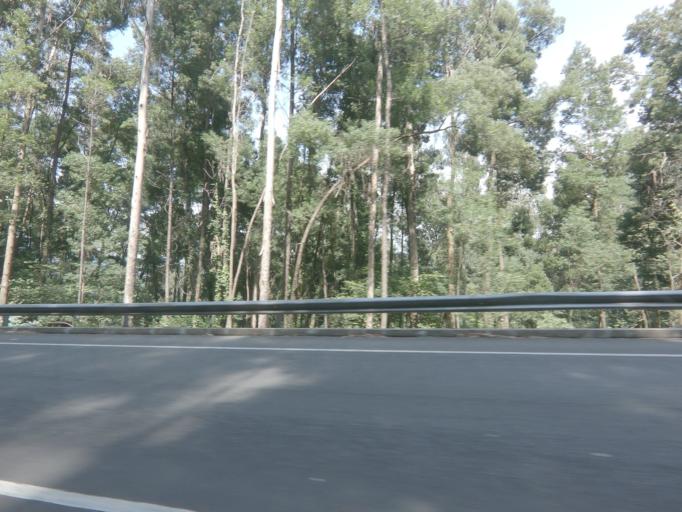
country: ES
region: Galicia
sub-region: Provincia de Pontevedra
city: Gondomar
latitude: 42.0921
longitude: -8.7538
